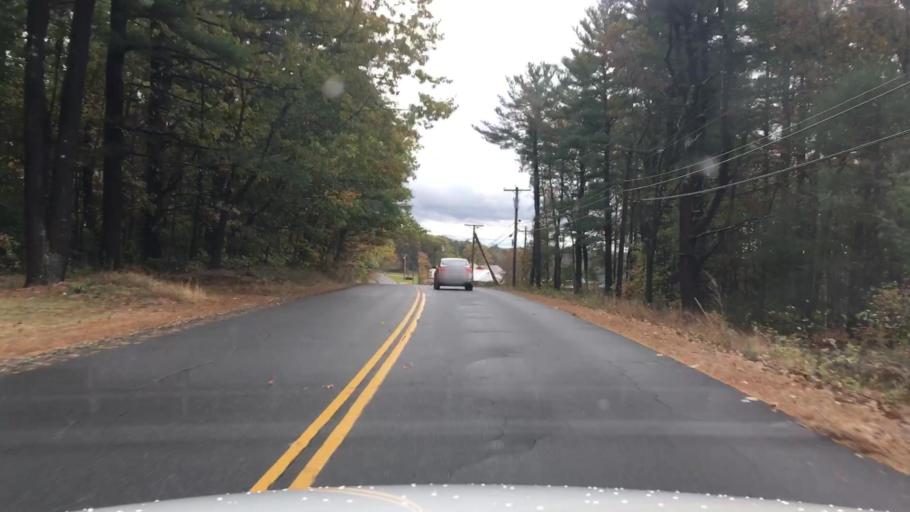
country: US
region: New Hampshire
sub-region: Strafford County
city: Lee
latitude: 43.0938
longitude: -70.9830
